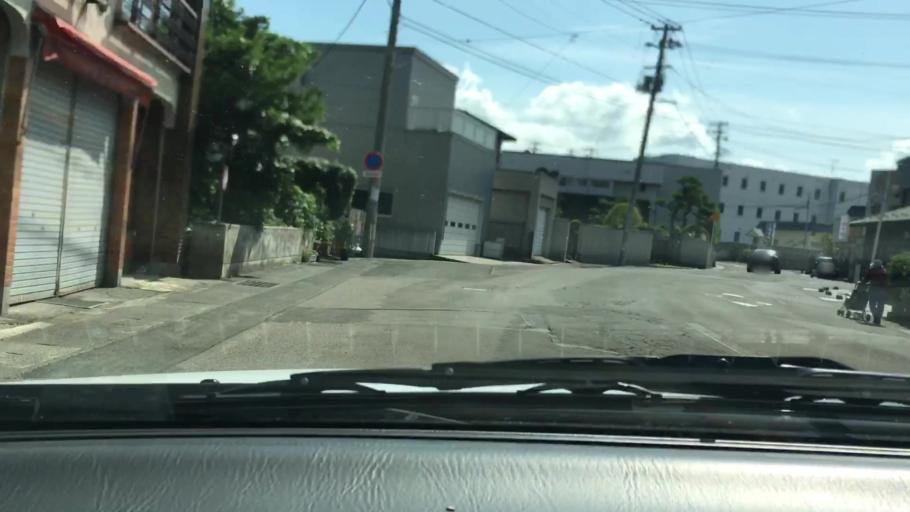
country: JP
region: Aomori
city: Hirosaki
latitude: 40.5958
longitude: 140.4711
